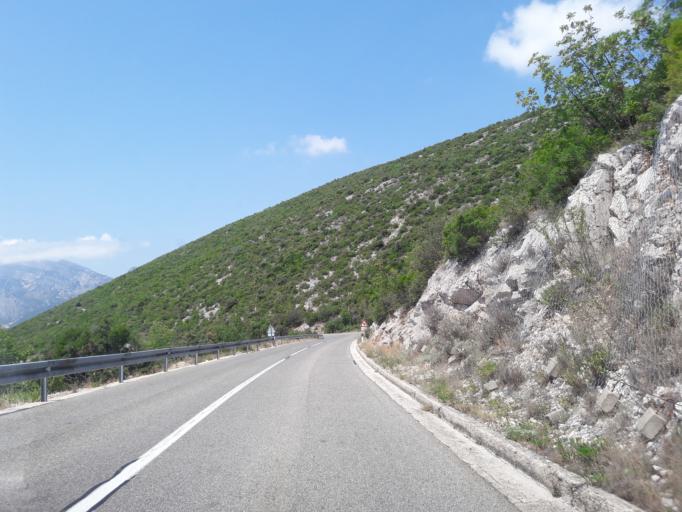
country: HR
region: Dubrovacko-Neretvanska
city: Orebic
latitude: 42.9688
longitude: 17.2533
